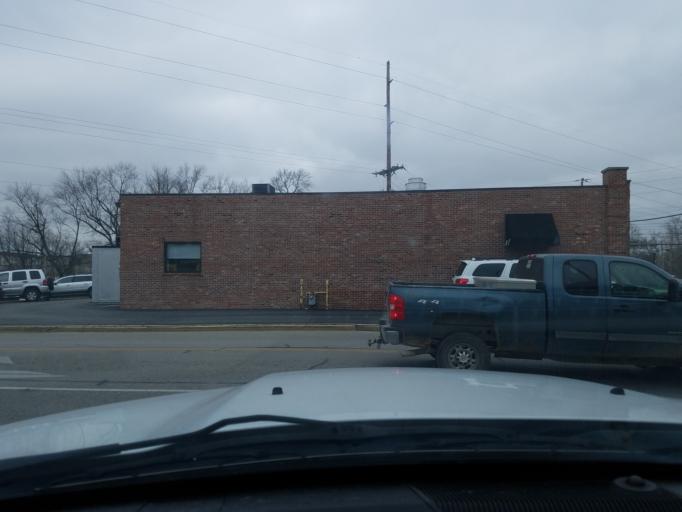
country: US
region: Indiana
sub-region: Dubois County
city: Jasper
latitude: 38.3864
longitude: -86.9273
